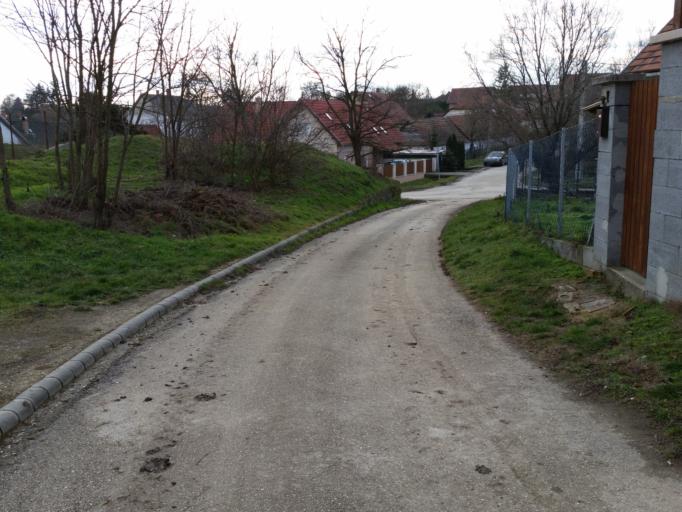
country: HU
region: Pest
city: Perbal
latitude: 47.5947
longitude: 18.7629
